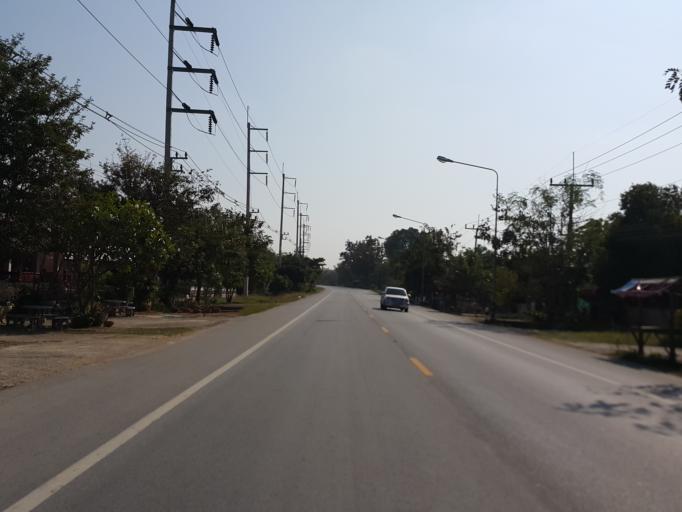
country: TH
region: Lampang
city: Chae Hom
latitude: 18.6770
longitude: 99.5486
